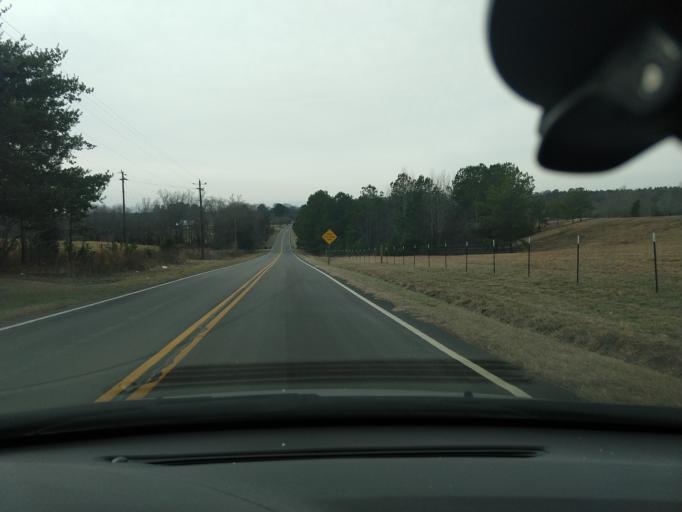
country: US
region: South Carolina
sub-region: Spartanburg County
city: Cowpens
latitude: 35.0477
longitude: -81.7915
